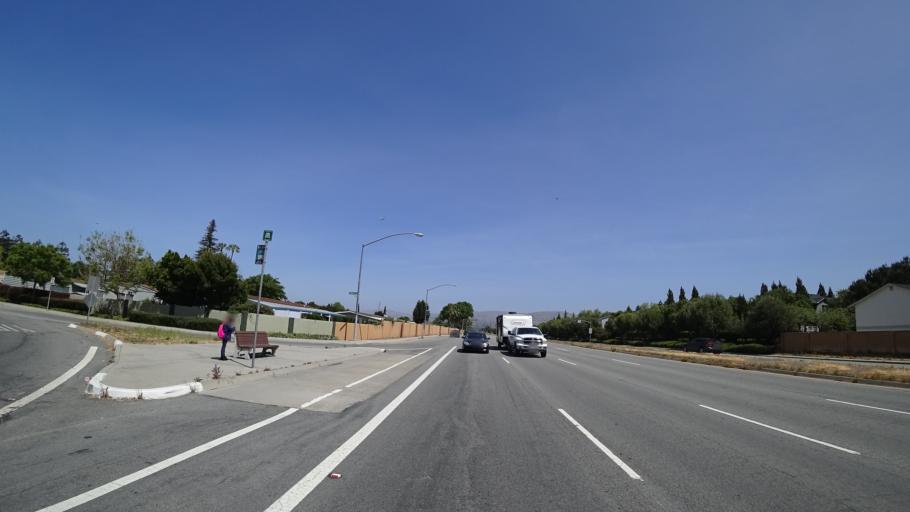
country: US
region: California
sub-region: Santa Clara County
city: Seven Trees
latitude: 37.3138
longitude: -121.8081
